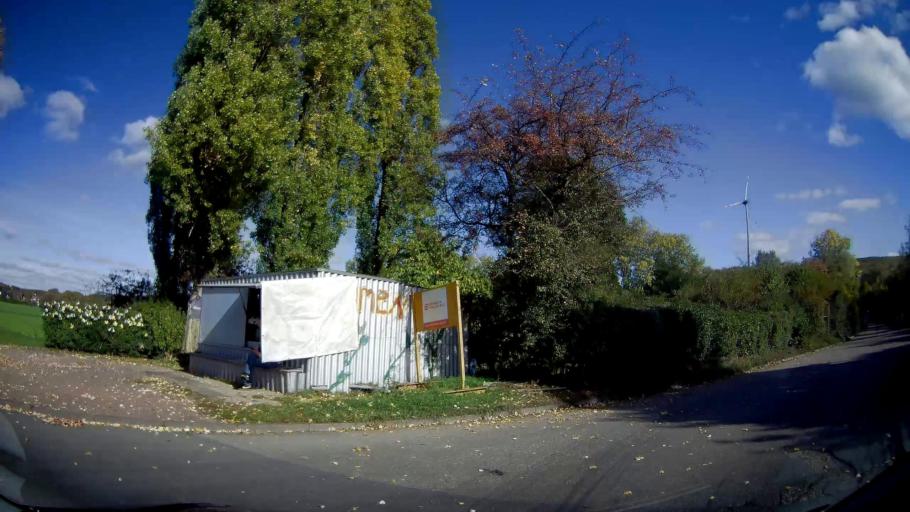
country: DE
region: North Rhine-Westphalia
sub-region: Regierungsbezirk Dusseldorf
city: Dinslaken
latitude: 51.5883
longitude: 6.7599
